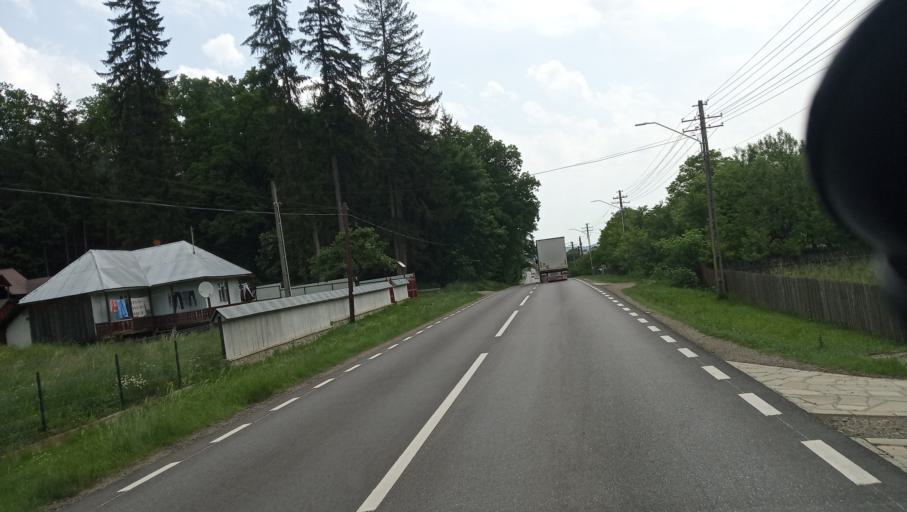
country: RO
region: Neamt
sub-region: Comuna Pipirig
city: Stanca
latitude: 47.2249
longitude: 26.1971
